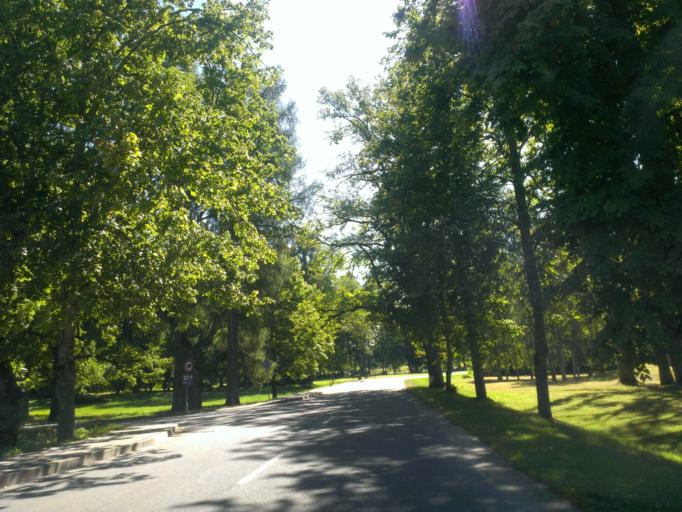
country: LV
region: Malpils
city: Malpils
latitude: 57.0090
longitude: 24.9501
